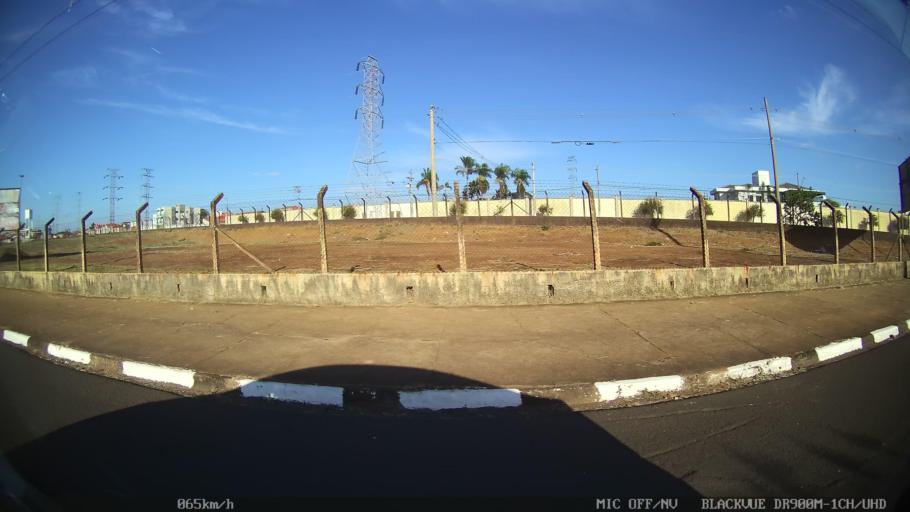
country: BR
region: Sao Paulo
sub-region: Franca
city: Franca
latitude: -20.5122
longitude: -47.3757
